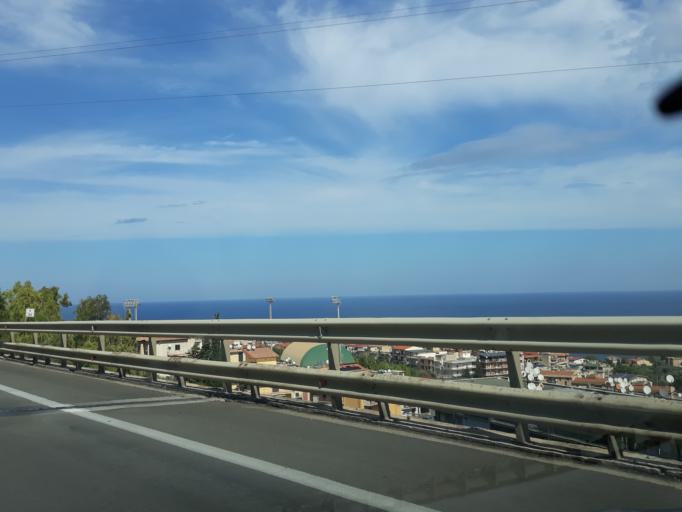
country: IT
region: Sicily
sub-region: Palermo
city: Trabia
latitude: 37.9862
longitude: 13.6567
